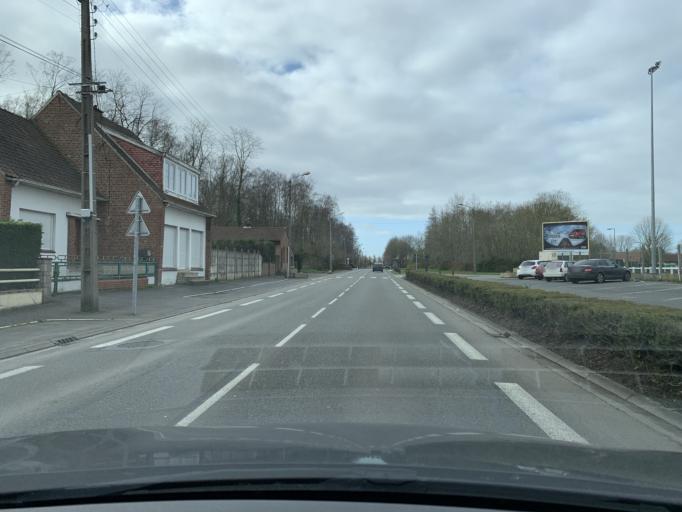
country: FR
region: Nord-Pas-de-Calais
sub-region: Departement du Nord
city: Roost-Warendin
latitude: 50.4061
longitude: 3.1073
